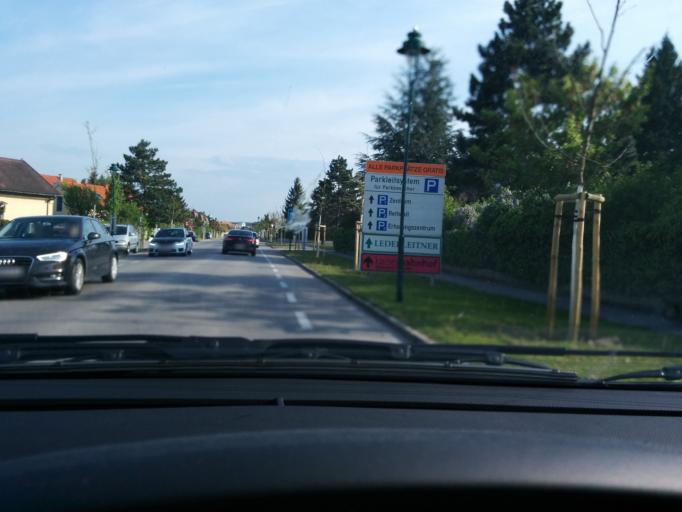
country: AT
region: Lower Austria
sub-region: Politischer Bezirk Modling
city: Laxenburg
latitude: 48.0749
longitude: 16.3534
